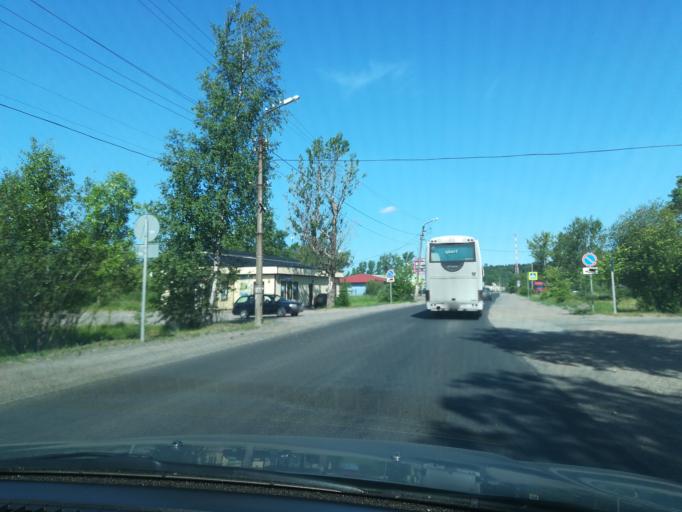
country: RU
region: Leningrad
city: Svetogorsk
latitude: 61.1158
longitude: 28.8516
